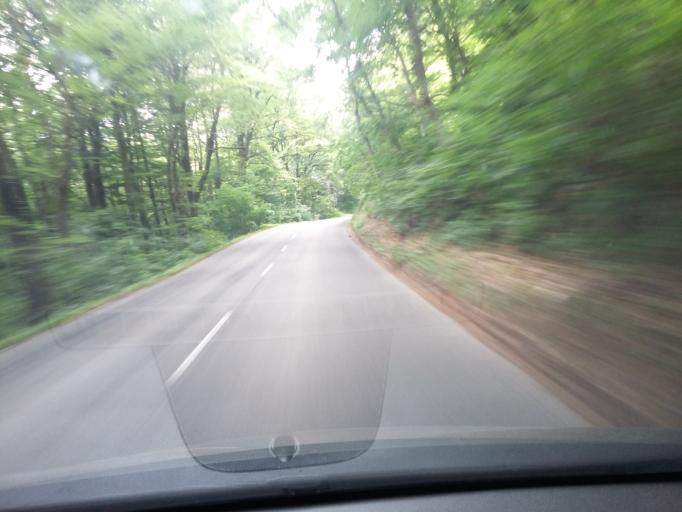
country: SK
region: Trnavsky
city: Smolenice
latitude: 48.5379
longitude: 17.3524
